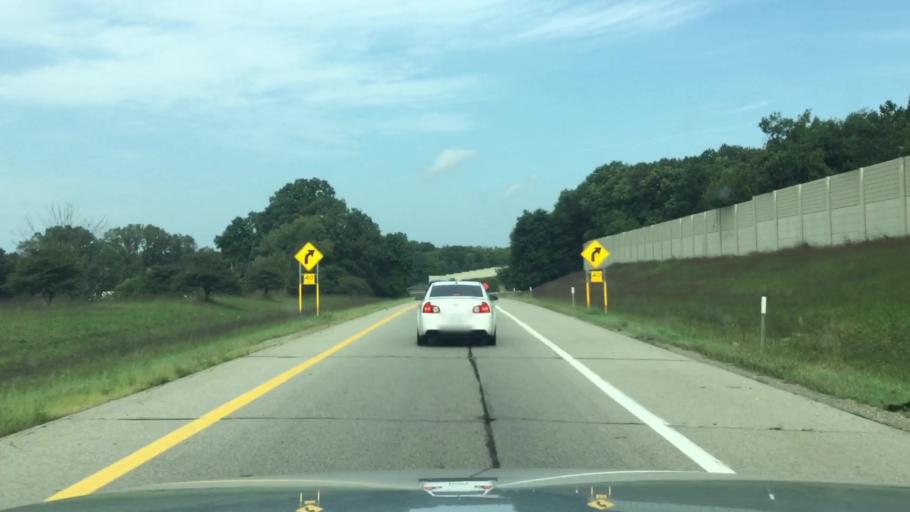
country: US
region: Michigan
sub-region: Kalamazoo County
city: Westwood
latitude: 42.2391
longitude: -85.6347
